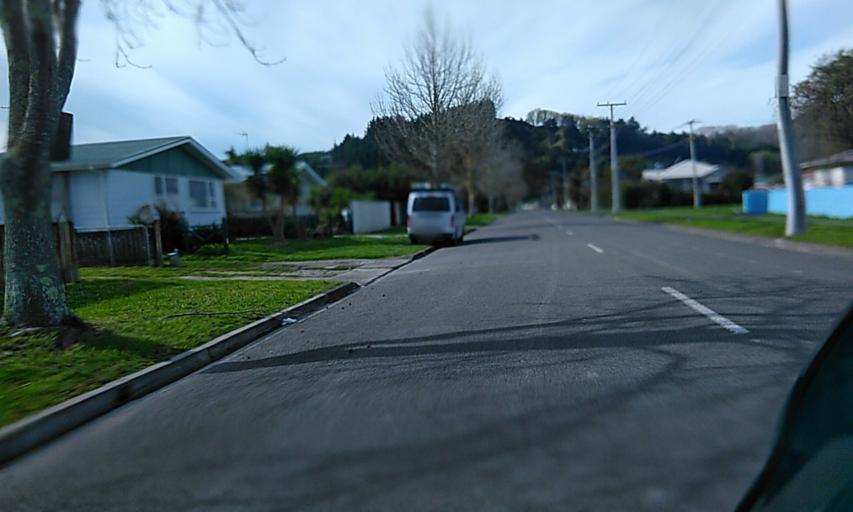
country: NZ
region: Gisborne
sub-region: Gisborne District
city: Gisborne
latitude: -38.6388
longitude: 178.0096
